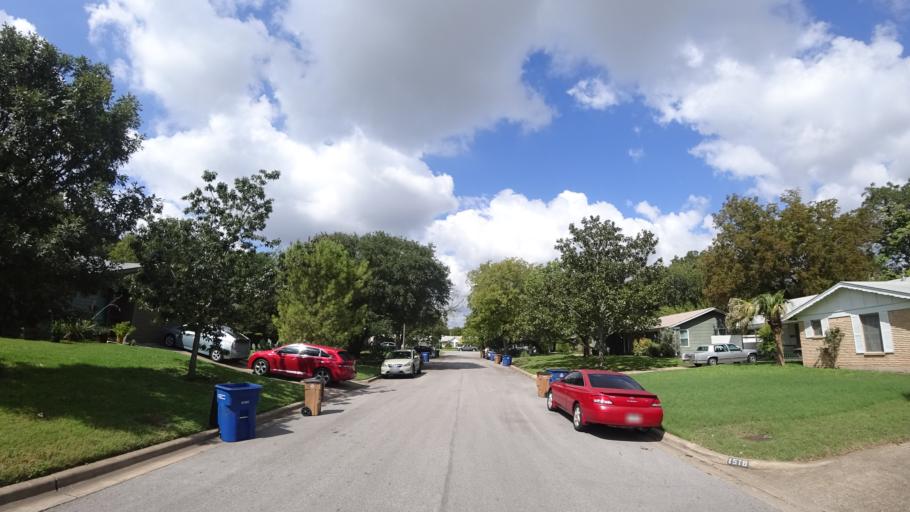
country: US
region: Texas
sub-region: Travis County
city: Wells Branch
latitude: 30.3604
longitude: -97.7198
